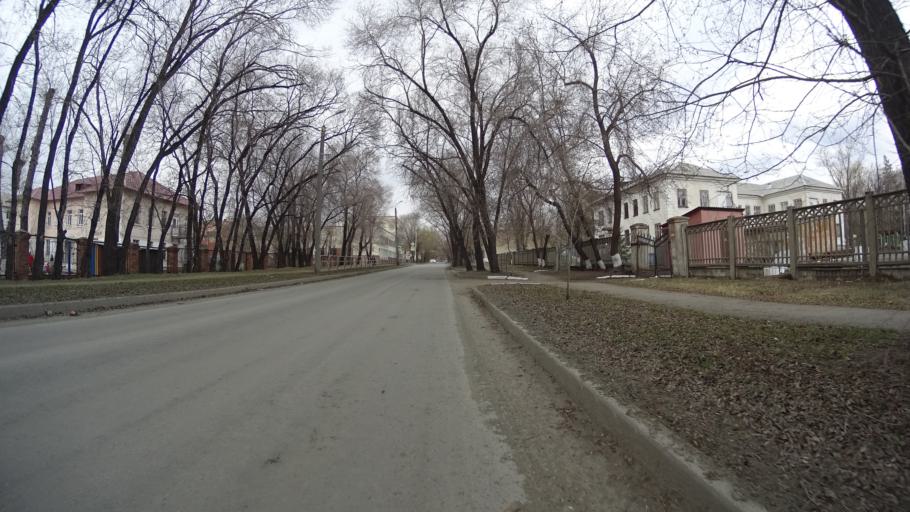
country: RU
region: Chelyabinsk
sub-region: Gorod Chelyabinsk
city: Chelyabinsk
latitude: 55.1648
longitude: 61.4380
